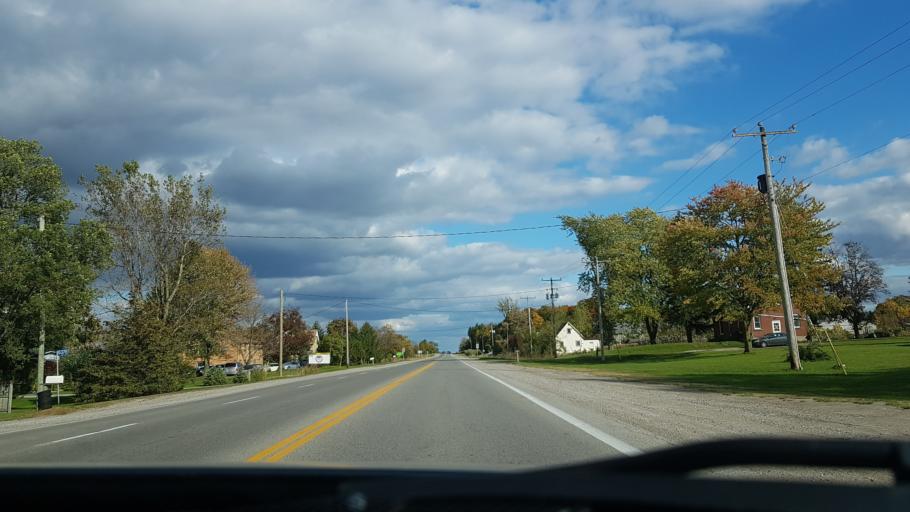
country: CA
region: Ontario
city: Delaware
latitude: 43.0002
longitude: -81.4212
